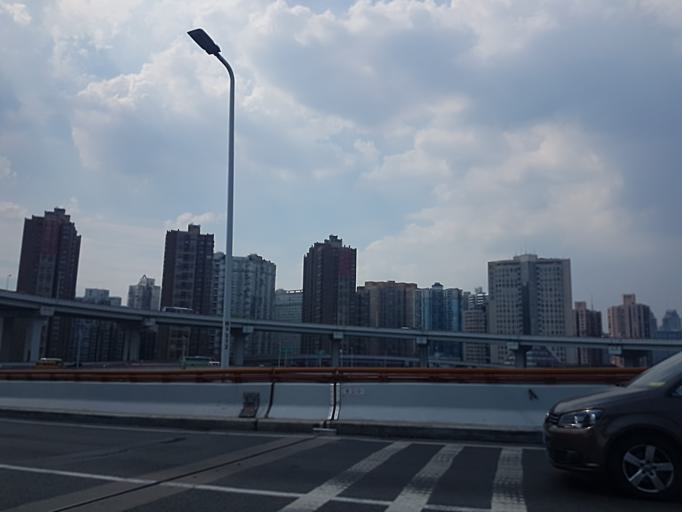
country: CN
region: Shanghai Shi
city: Luwan
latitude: 31.2093
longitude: 121.4977
